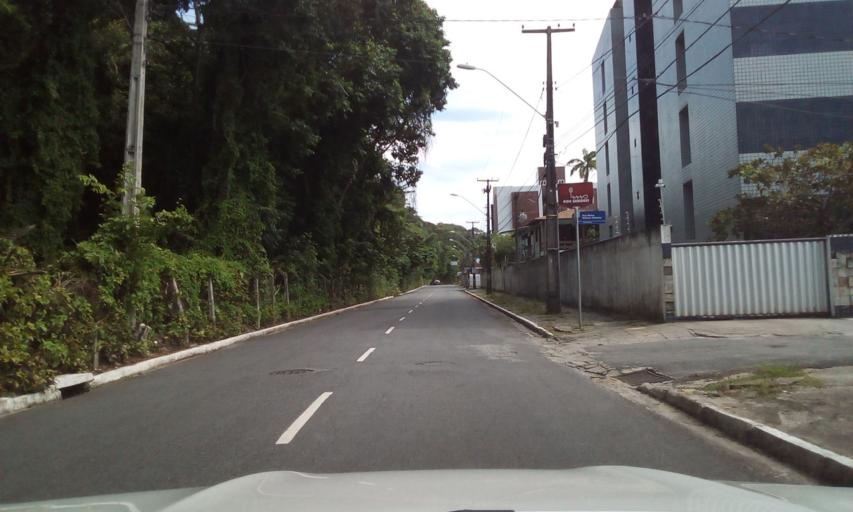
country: BR
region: Paraiba
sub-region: Joao Pessoa
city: Joao Pessoa
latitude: -7.1450
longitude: -34.8128
